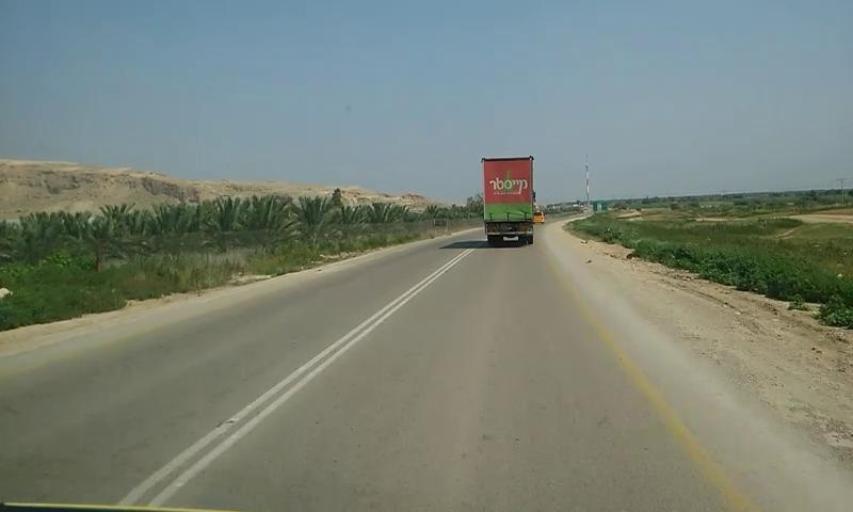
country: PS
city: Al Jiftlik
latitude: 32.1218
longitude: 35.5053
